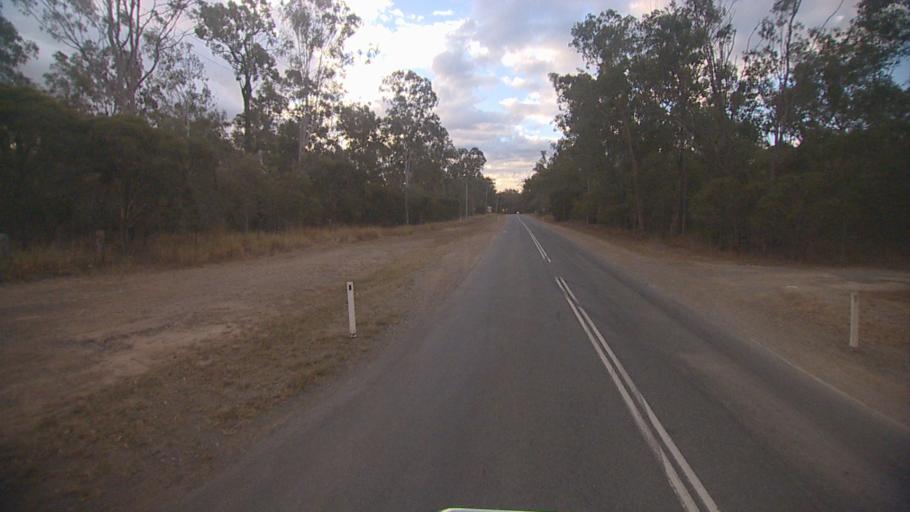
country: AU
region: Queensland
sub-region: Logan
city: Cedar Vale
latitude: -27.8424
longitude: 153.0483
